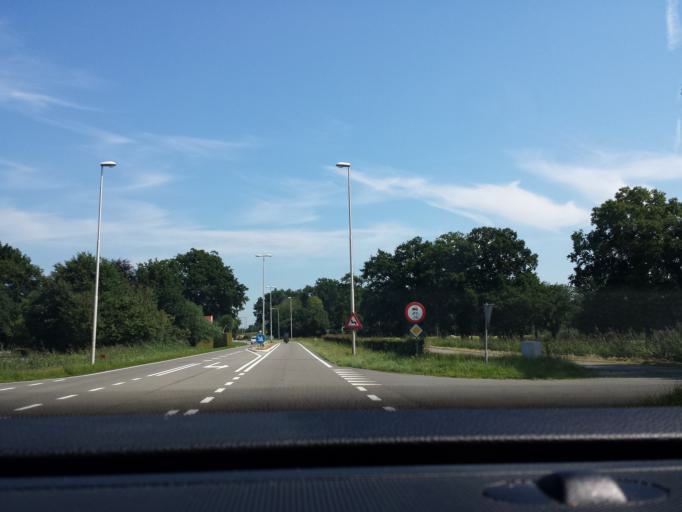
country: NL
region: Overijssel
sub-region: Gemeente Hof van Twente
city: Hengevelde
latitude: 52.2492
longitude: 6.6434
